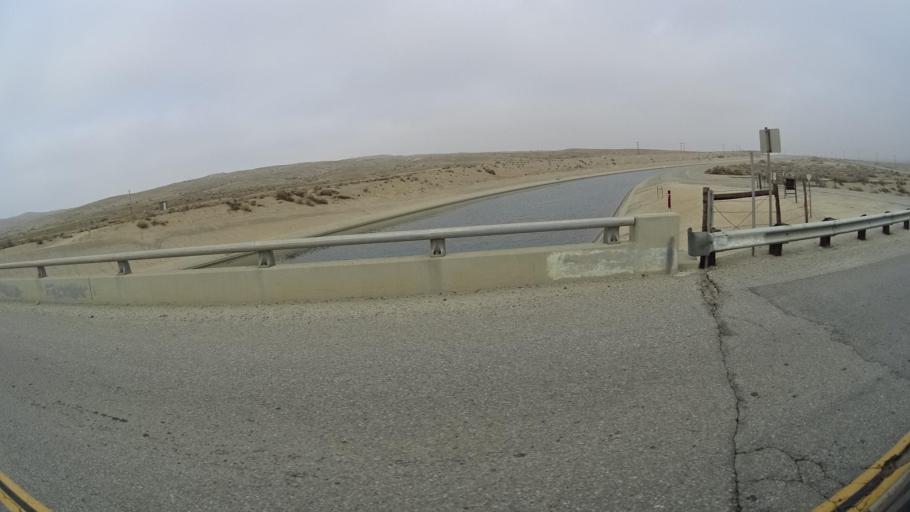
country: US
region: California
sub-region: Kern County
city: Maricopa
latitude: 35.1296
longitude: -119.3682
